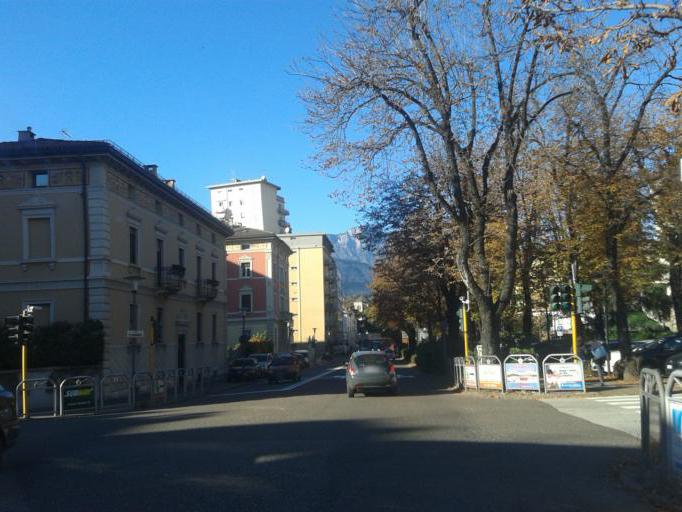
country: IT
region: Trentino-Alto Adige
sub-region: Provincia di Trento
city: Trento
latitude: 46.0598
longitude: 11.1261
